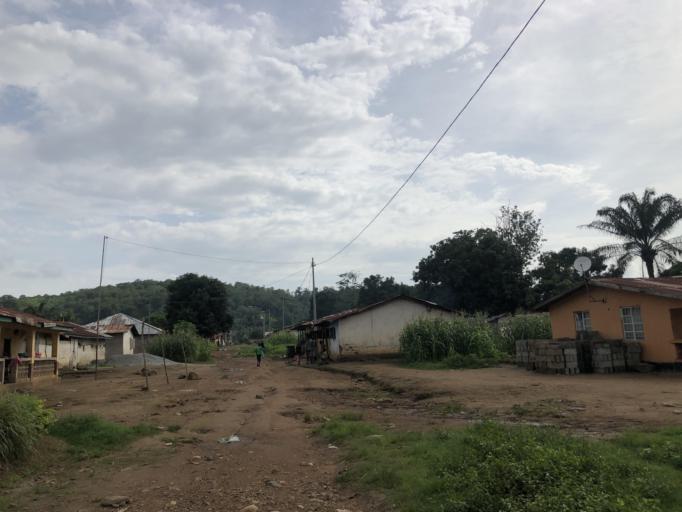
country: SL
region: Northern Province
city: Bumbuna
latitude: 9.0447
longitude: -11.7427
